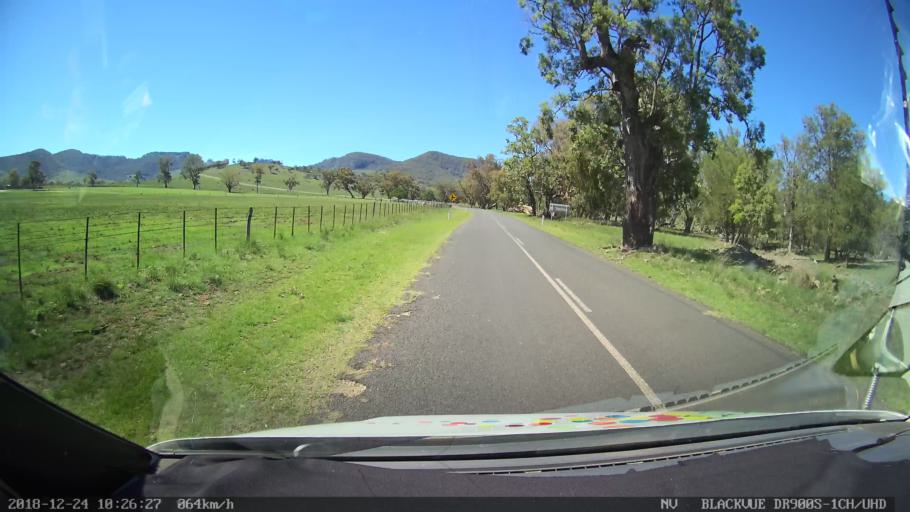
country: AU
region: New South Wales
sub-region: Liverpool Plains
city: Quirindi
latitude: -31.8095
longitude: 150.5274
